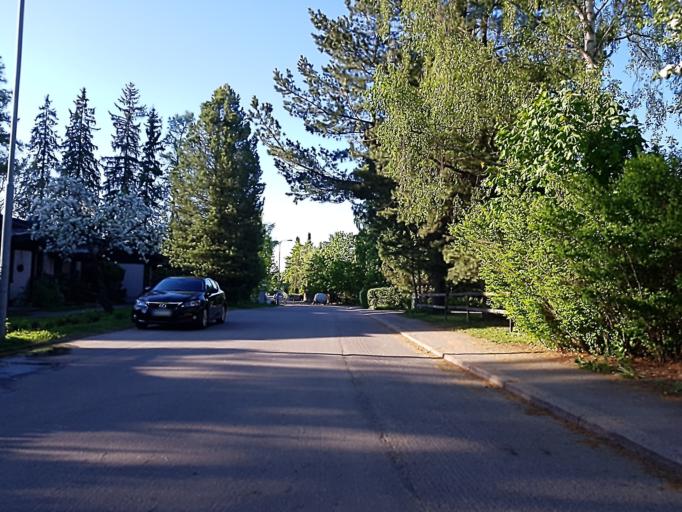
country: FI
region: Uusimaa
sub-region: Helsinki
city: Helsinki
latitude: 60.2488
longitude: 24.9518
